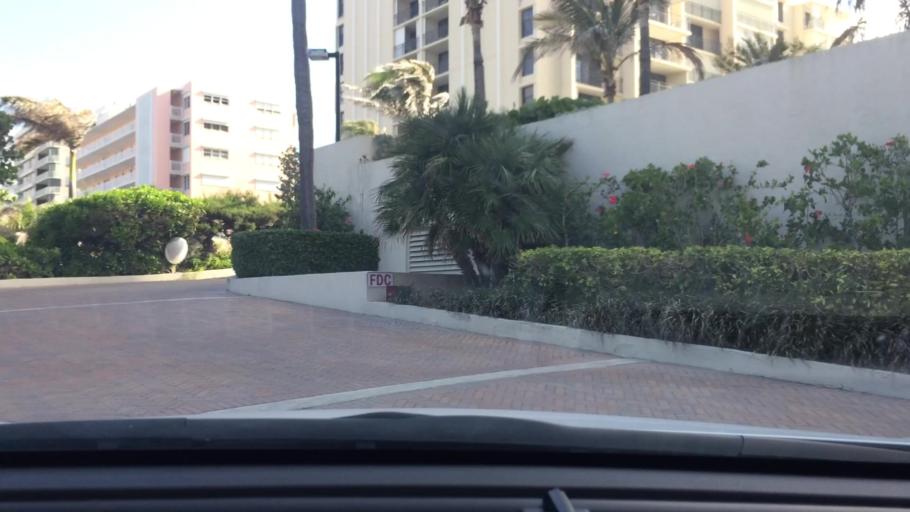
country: US
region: Florida
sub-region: Palm Beach County
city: Highland Beach
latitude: 26.4204
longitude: -80.0642
